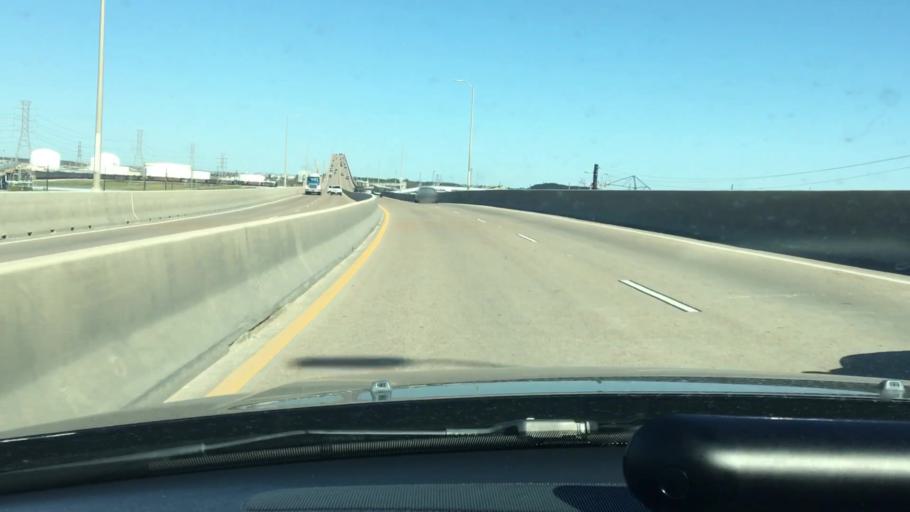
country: US
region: Texas
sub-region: Harris County
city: Deer Park
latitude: 29.7218
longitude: -95.1479
